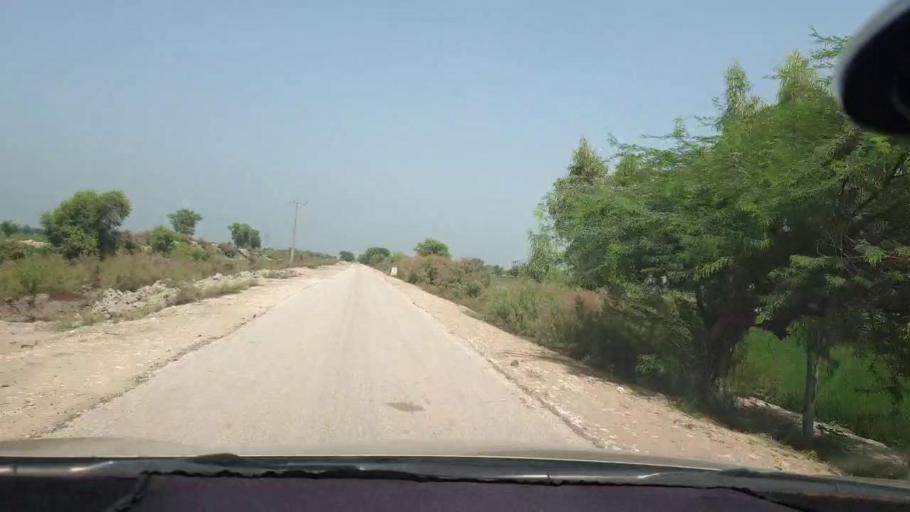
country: PK
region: Sindh
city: Kambar
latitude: 27.6646
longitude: 67.8902
